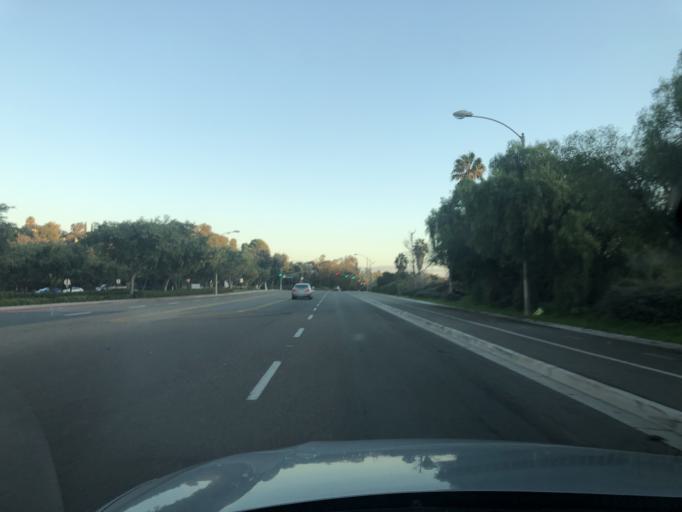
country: US
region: California
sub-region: San Diego County
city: Chula Vista
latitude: 32.6531
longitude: -117.0662
